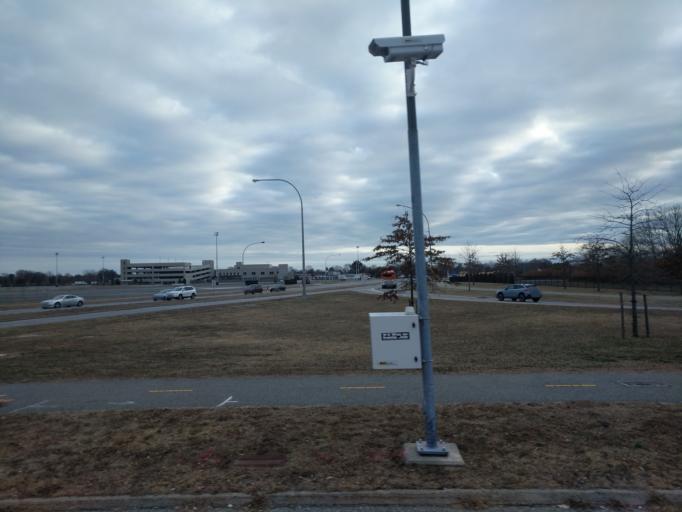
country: US
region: New York
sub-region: Nassau County
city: East Garden City
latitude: 40.7229
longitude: -73.5940
